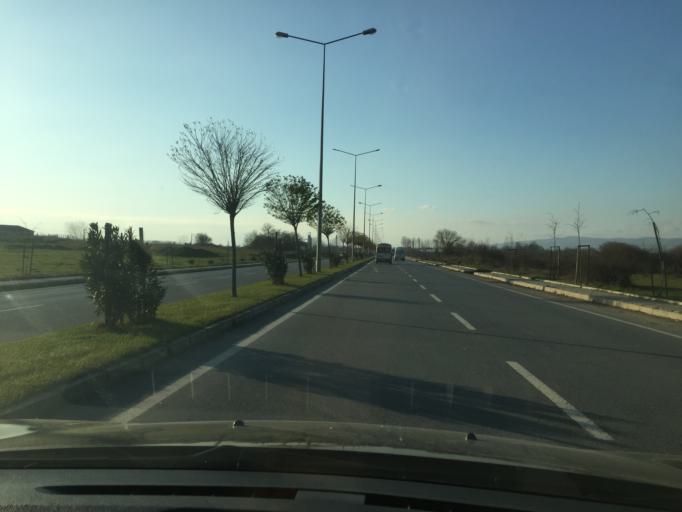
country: TR
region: Sakarya
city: Sogutlu
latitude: 40.9030
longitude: 30.4969
